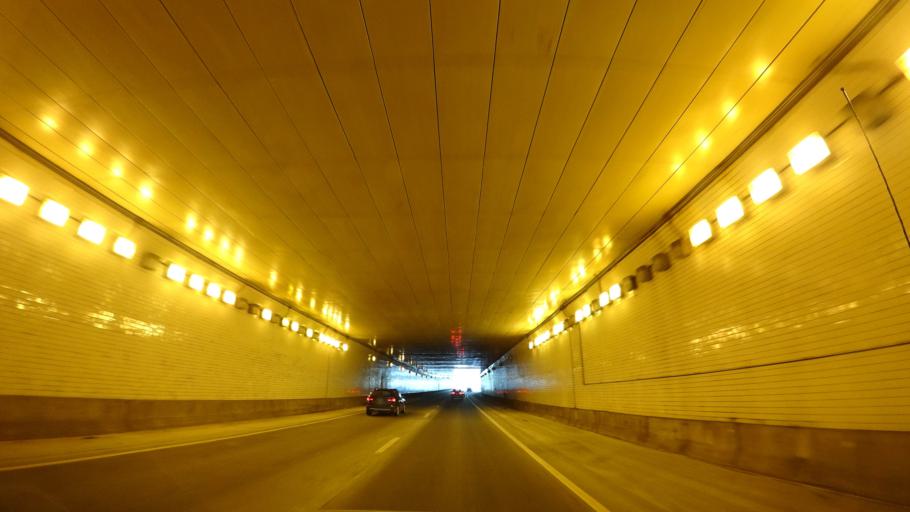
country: US
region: Virginia
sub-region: Arlington County
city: Arlington
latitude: 38.8986
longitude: -77.0726
